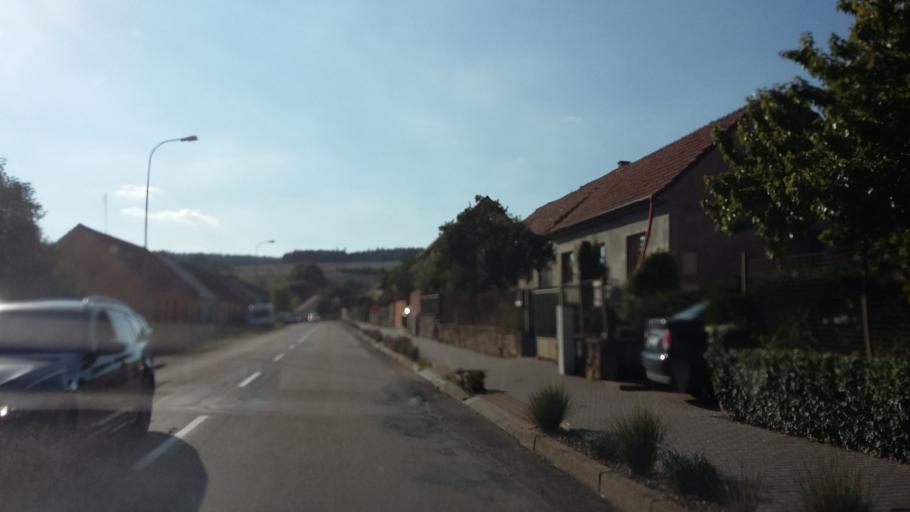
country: CZ
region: South Moravian
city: Ricany
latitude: 49.2154
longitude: 16.3906
